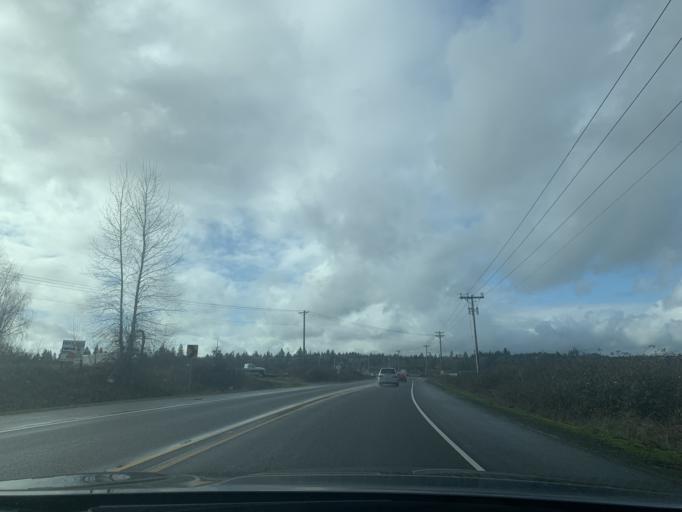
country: US
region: Oregon
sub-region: Washington County
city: Sherwood
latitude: 45.3827
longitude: -122.8532
